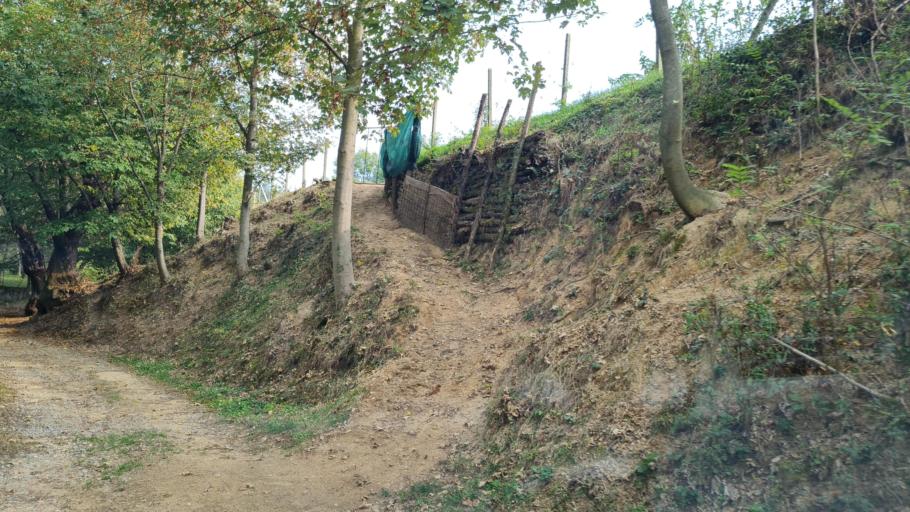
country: IT
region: Piedmont
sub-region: Provincia di Biella
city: Mezzana Mortigliengo
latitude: 45.6251
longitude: 8.1962
